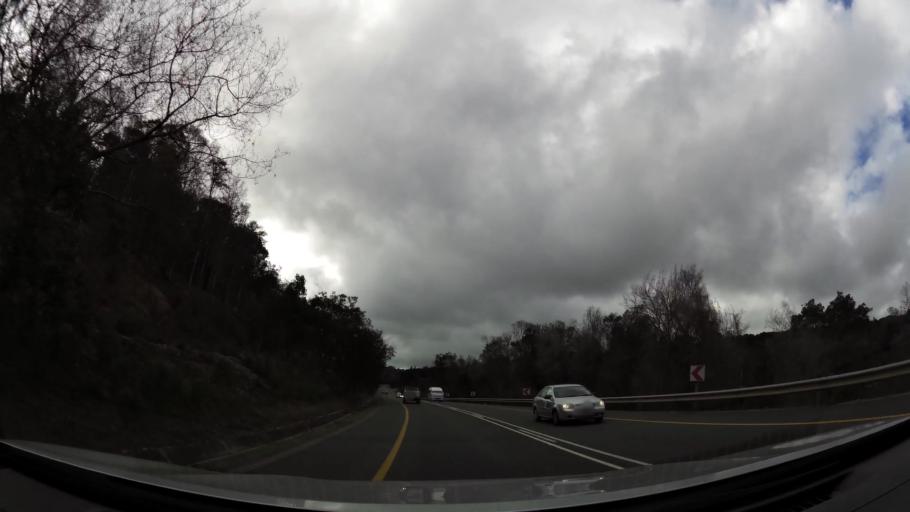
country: ZA
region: Western Cape
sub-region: Eden District Municipality
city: Knysna
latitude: -34.0336
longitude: 23.1585
